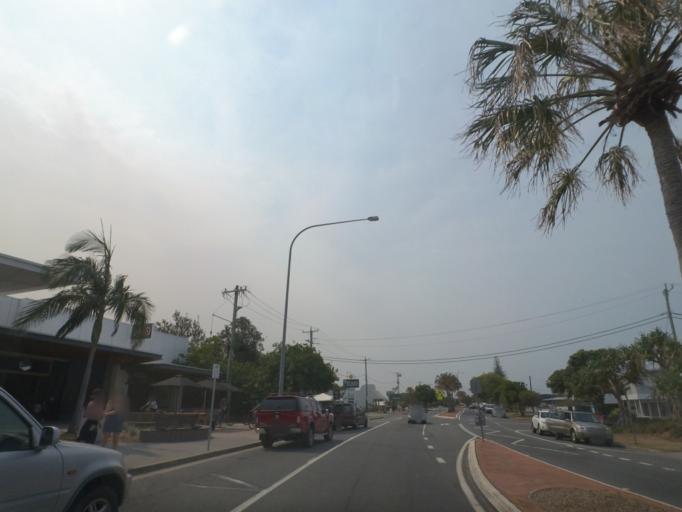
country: AU
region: New South Wales
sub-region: Tweed
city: Casuarina
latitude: -28.3319
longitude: 153.5695
